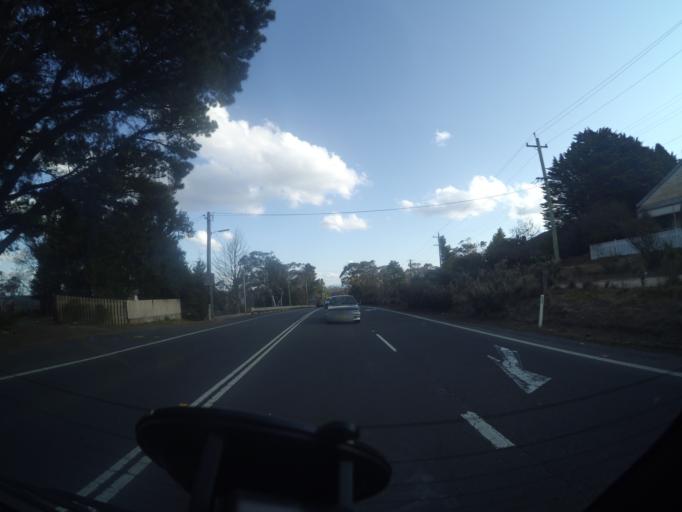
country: AU
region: New South Wales
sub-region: Blue Mountains Municipality
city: Blackheath
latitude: -33.6424
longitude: 150.2850
